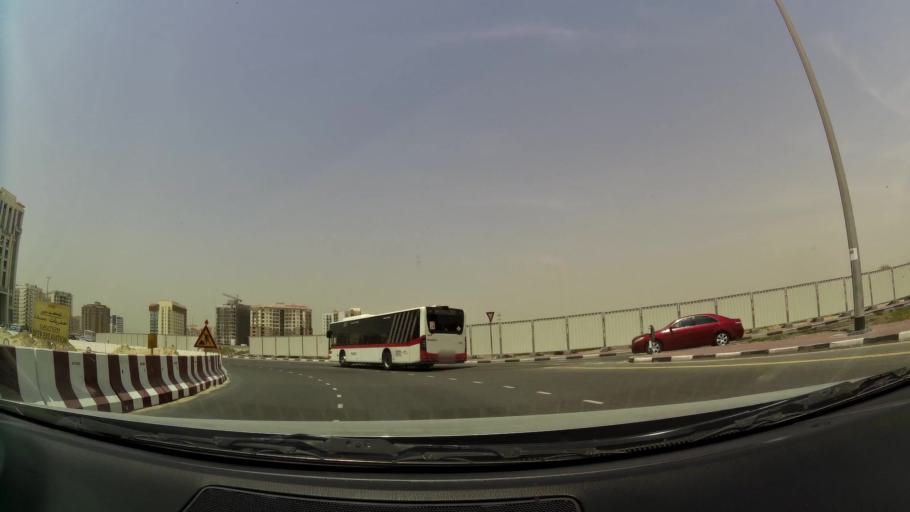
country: AE
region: Ash Shariqah
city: Sharjah
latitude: 25.1631
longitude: 55.4077
